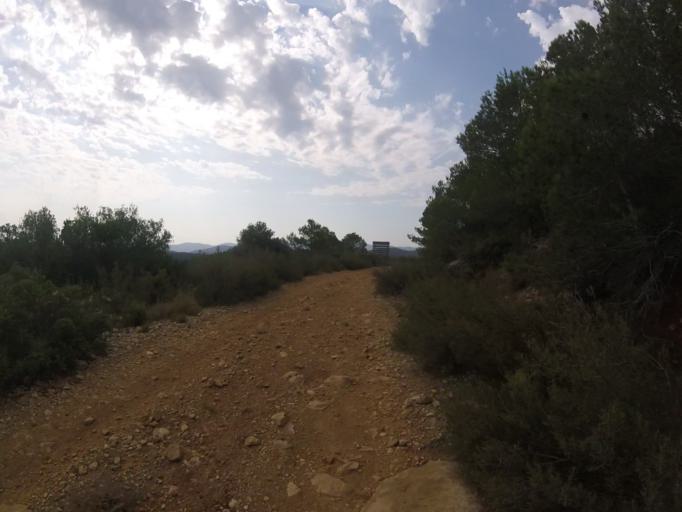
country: ES
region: Valencia
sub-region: Provincia de Castello
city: Alcala de Xivert
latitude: 40.3823
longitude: 0.2071
